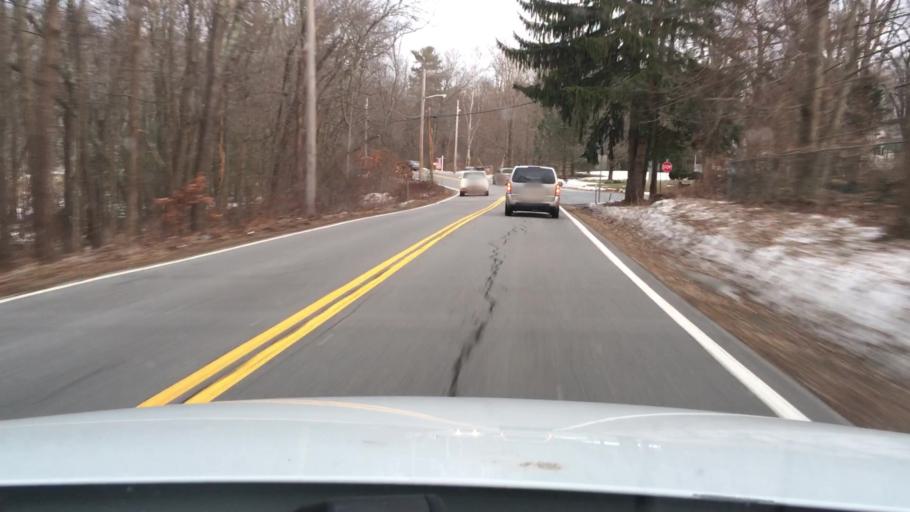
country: US
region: New Hampshire
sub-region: Rockingham County
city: Atkinson
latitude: 42.8288
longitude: -71.1385
